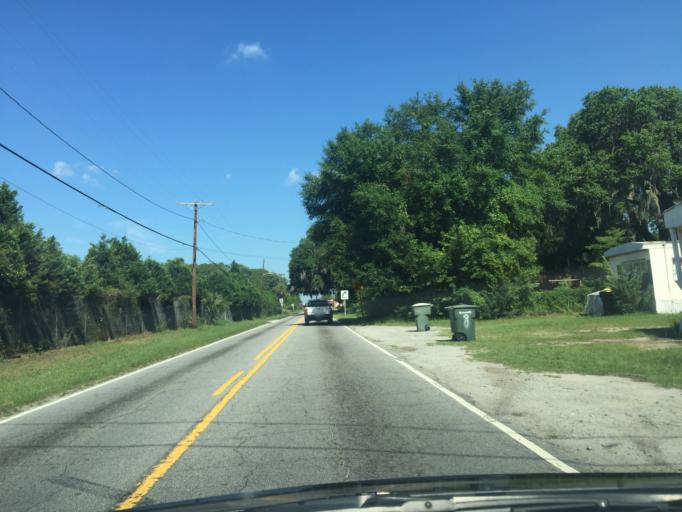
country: US
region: Georgia
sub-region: Chatham County
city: Savannah
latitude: 32.0272
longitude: -81.1186
